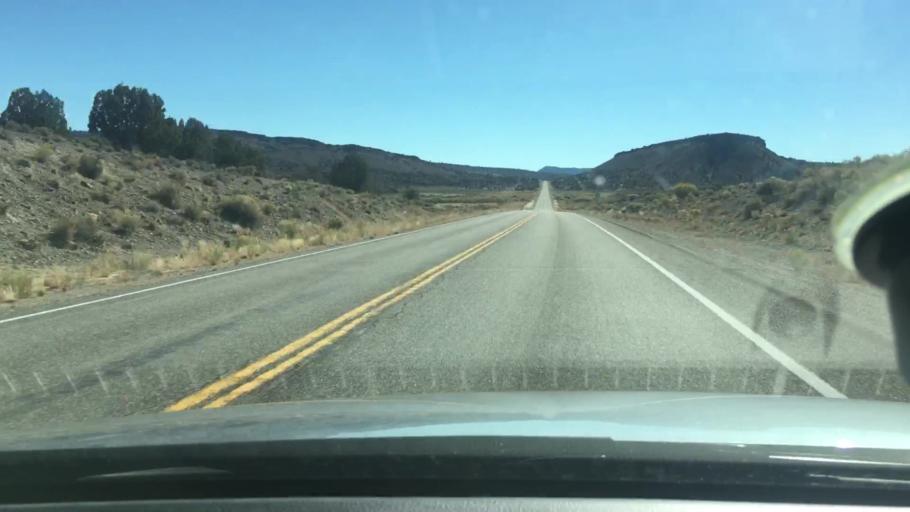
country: US
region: Nevada
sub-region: White Pine County
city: Ely
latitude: 38.9329
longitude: -115.1715
